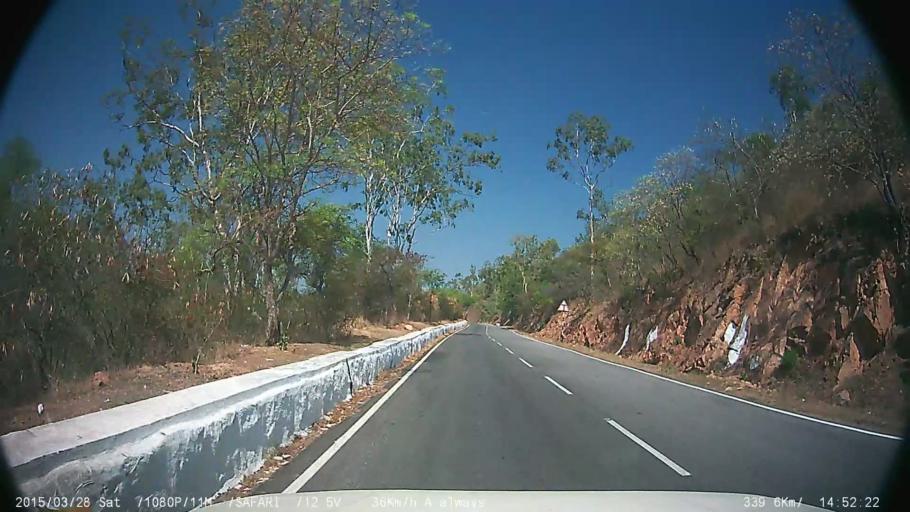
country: IN
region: Karnataka
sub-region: Mysore
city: Mysore
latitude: 12.2847
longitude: 76.6888
